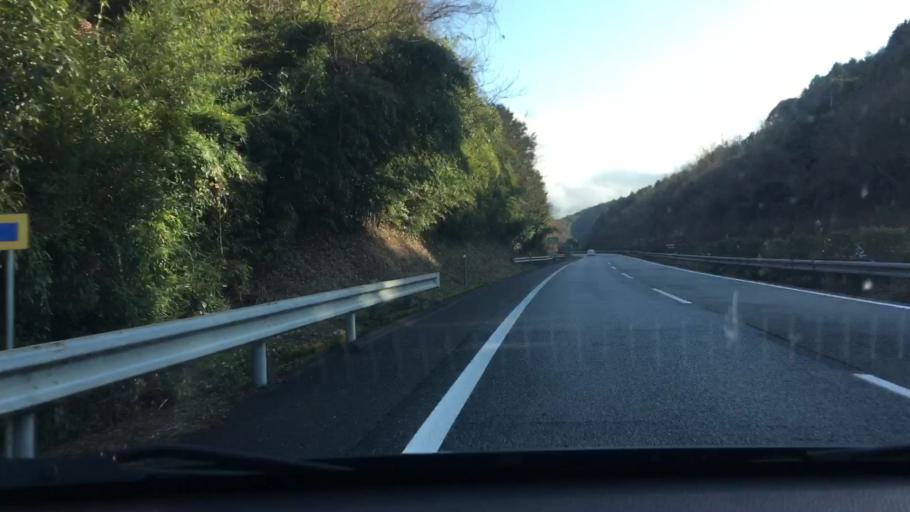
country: JP
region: Kumamoto
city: Hitoyoshi
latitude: 32.1748
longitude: 130.7897
